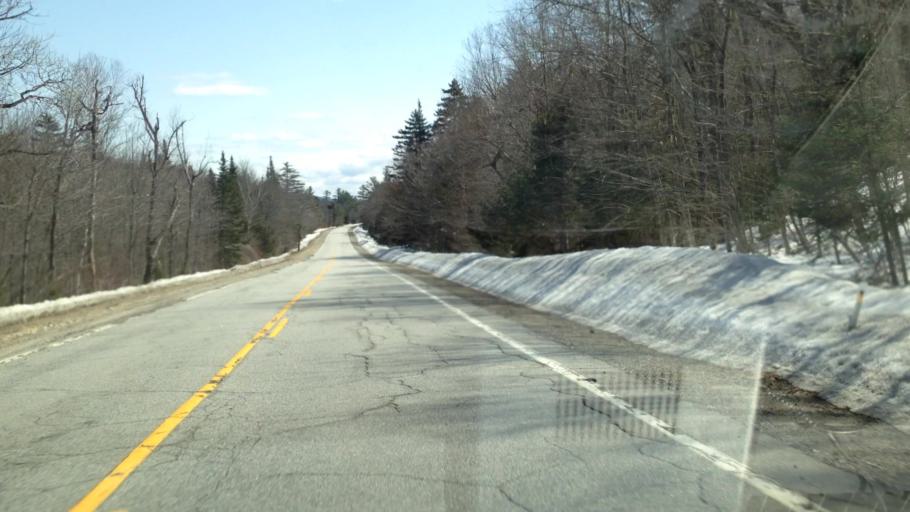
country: US
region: New Hampshire
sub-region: Sullivan County
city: Springfield
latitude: 43.4958
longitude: -72.0018
